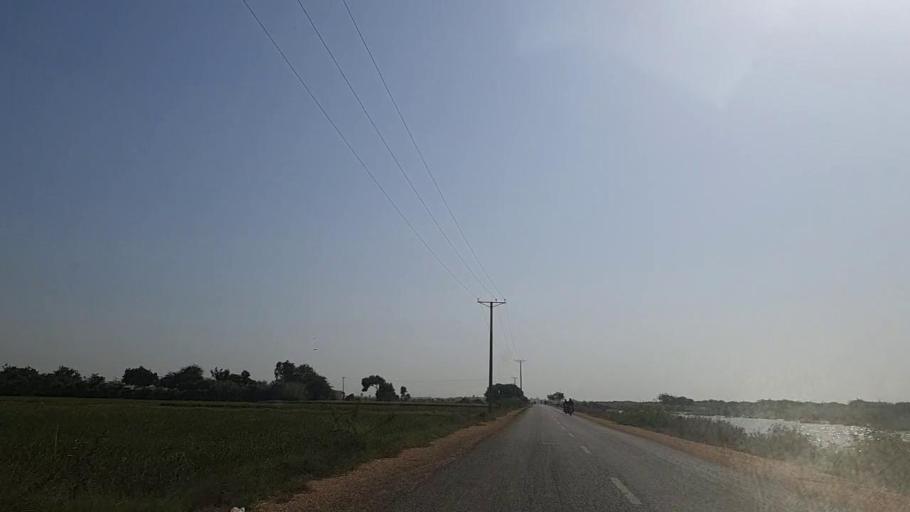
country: PK
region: Sindh
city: Jati
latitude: 24.5413
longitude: 68.2799
